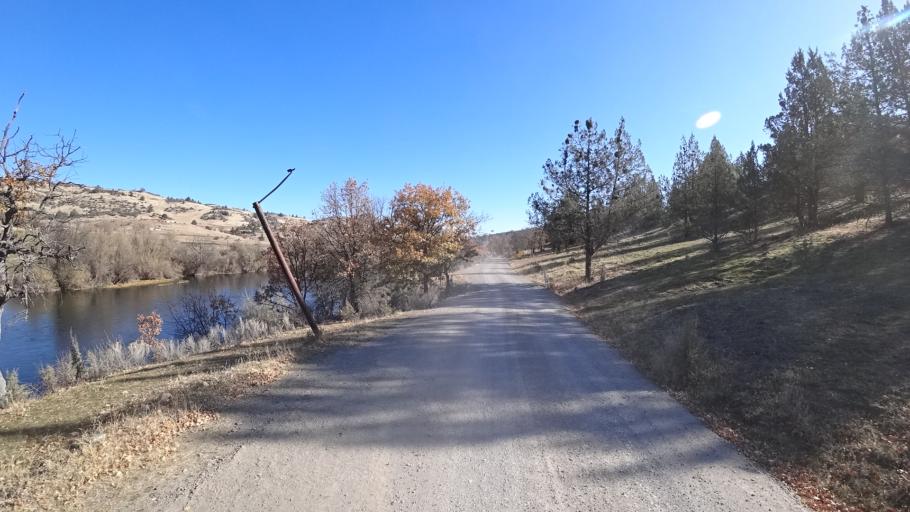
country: US
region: California
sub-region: Siskiyou County
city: Montague
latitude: 41.8937
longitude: -122.5273
